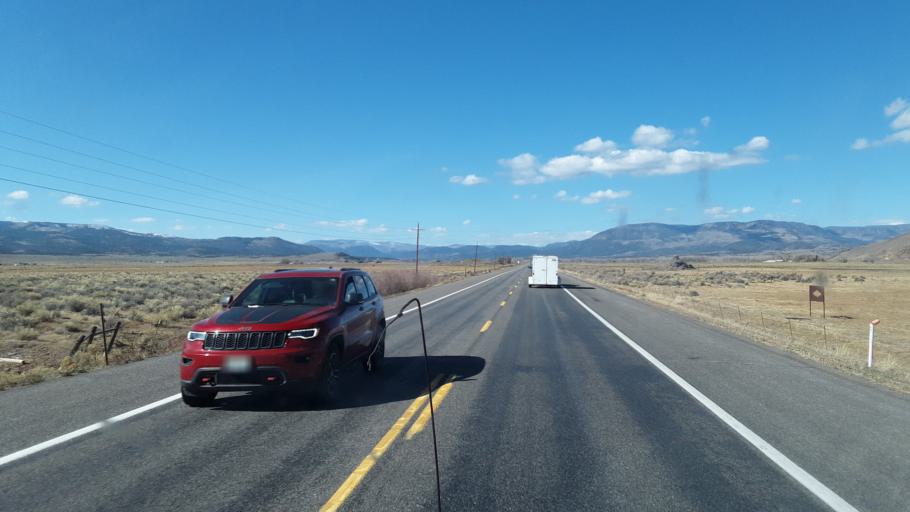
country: US
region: Colorado
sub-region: Rio Grande County
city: Del Norte
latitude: 37.6742
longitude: -106.4172
